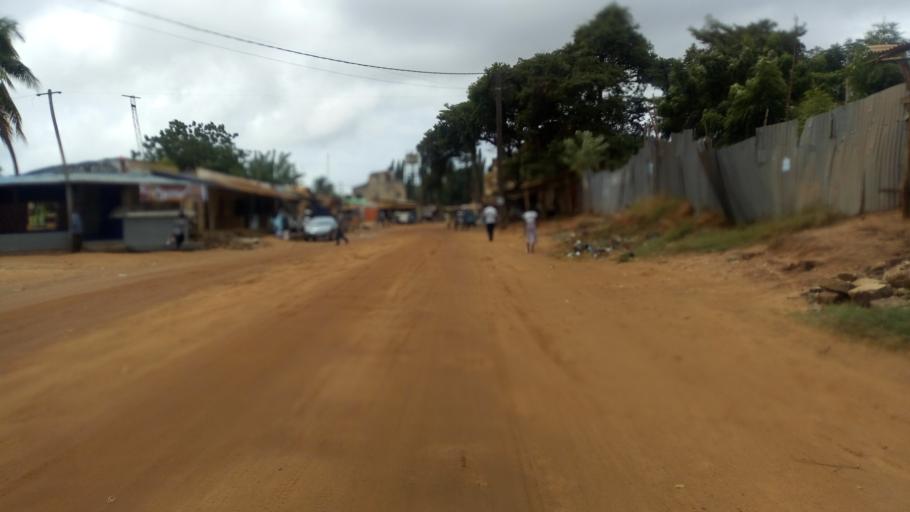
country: TG
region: Maritime
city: Lome
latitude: 6.1804
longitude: 1.1682
